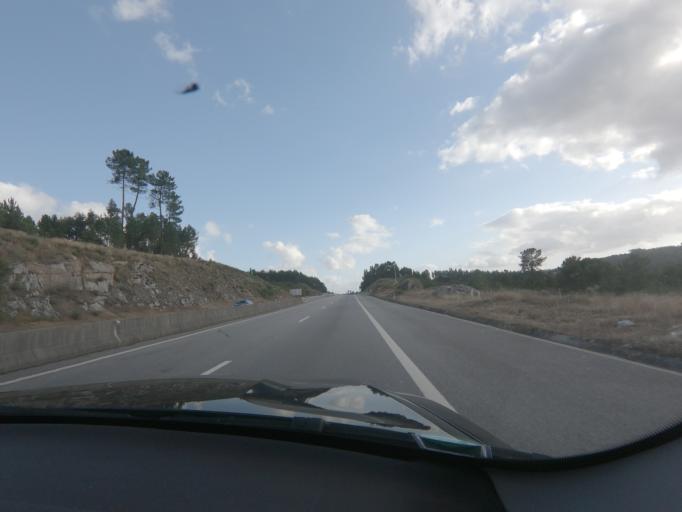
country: PT
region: Viseu
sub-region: Viseu
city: Viseu
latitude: 40.6337
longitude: -7.9586
